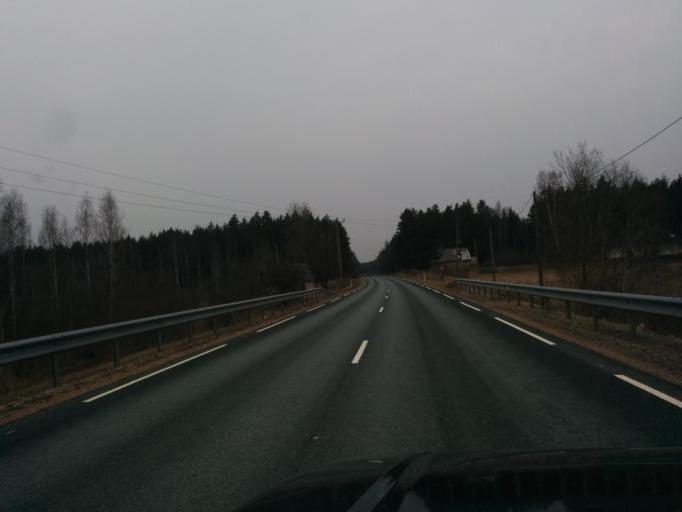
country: LV
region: Ogre
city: Ogre
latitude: 56.7905
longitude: 24.6052
